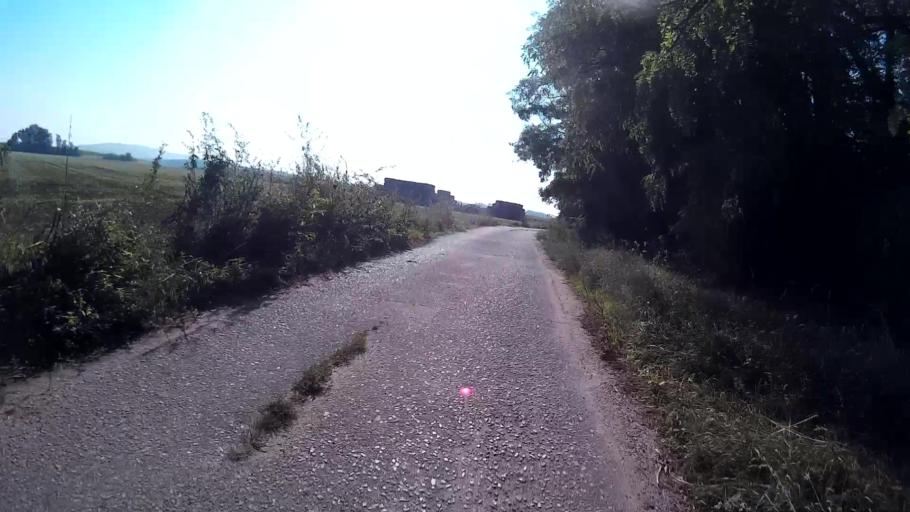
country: CZ
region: South Moravian
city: Vranovice
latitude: 48.9481
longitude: 16.5767
